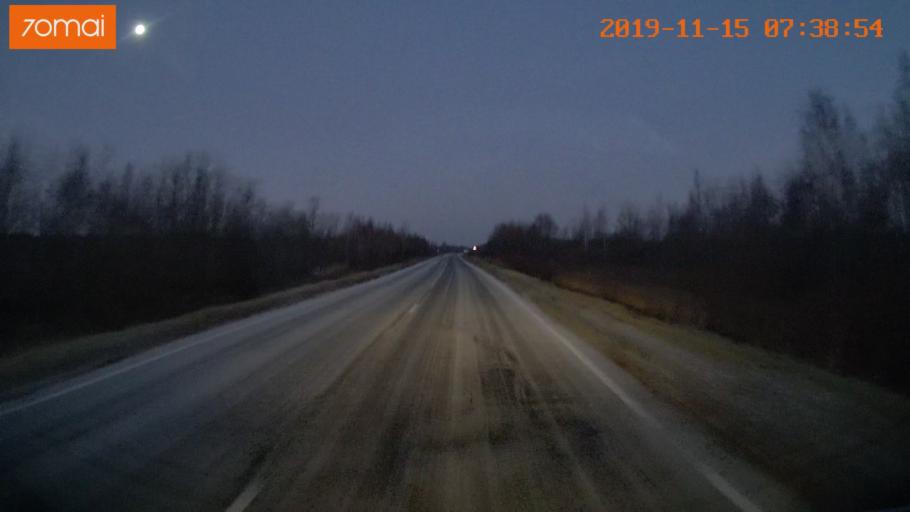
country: RU
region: Vologda
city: Sheksna
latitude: 58.7623
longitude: 38.3907
